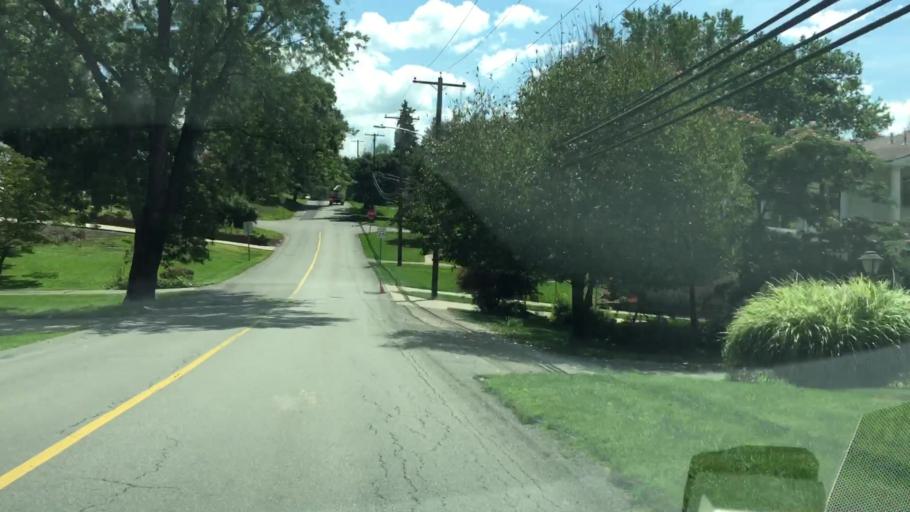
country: US
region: Pennsylvania
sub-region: Allegheny County
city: Bethel Park
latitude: 40.3206
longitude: -80.0538
